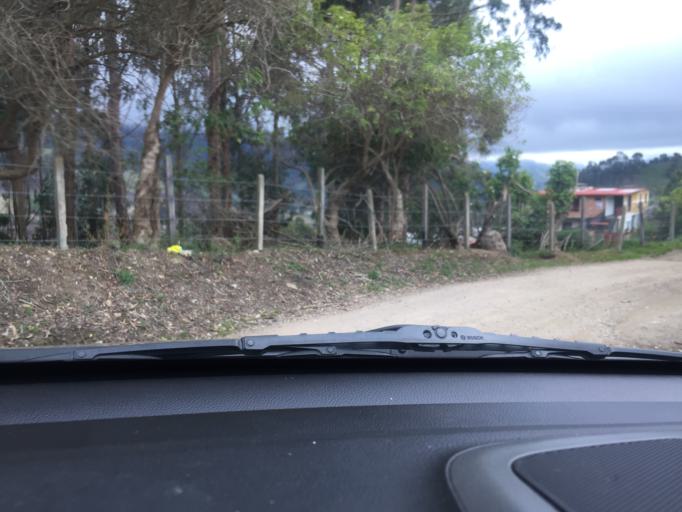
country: CO
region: Cundinamarca
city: Zipacon
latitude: 4.7622
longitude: -74.3776
